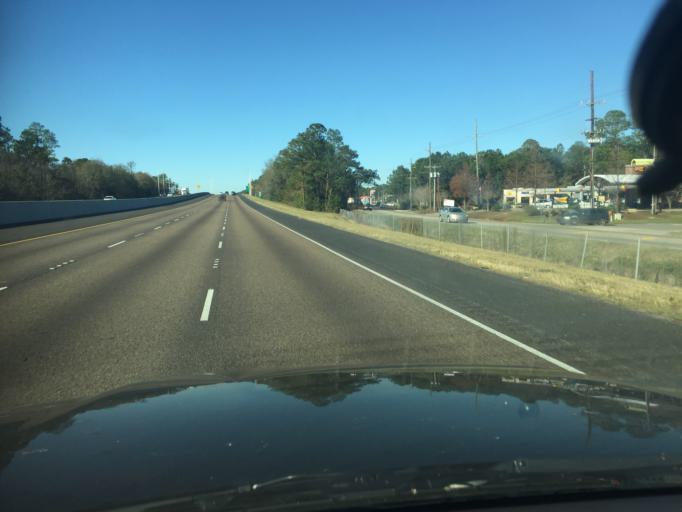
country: US
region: Louisiana
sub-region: Saint Tammany Parish
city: Slidell
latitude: 30.3103
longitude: -89.7648
